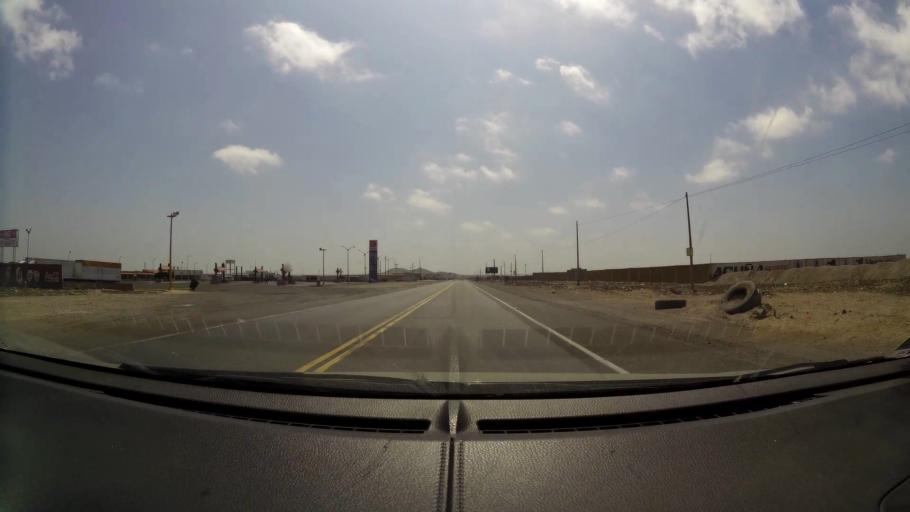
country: PE
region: Lambayeque
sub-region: Provincia de Chiclayo
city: Reque
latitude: -6.8955
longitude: -79.7928
